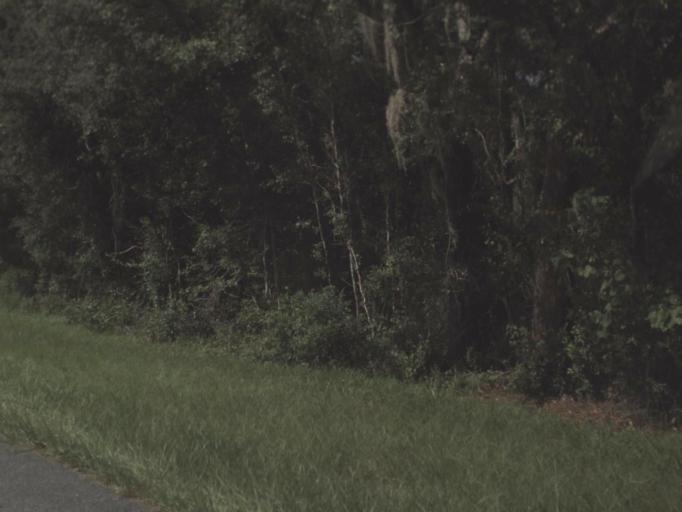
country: US
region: Florida
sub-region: Citrus County
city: Hernando
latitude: 28.9241
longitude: -82.3902
